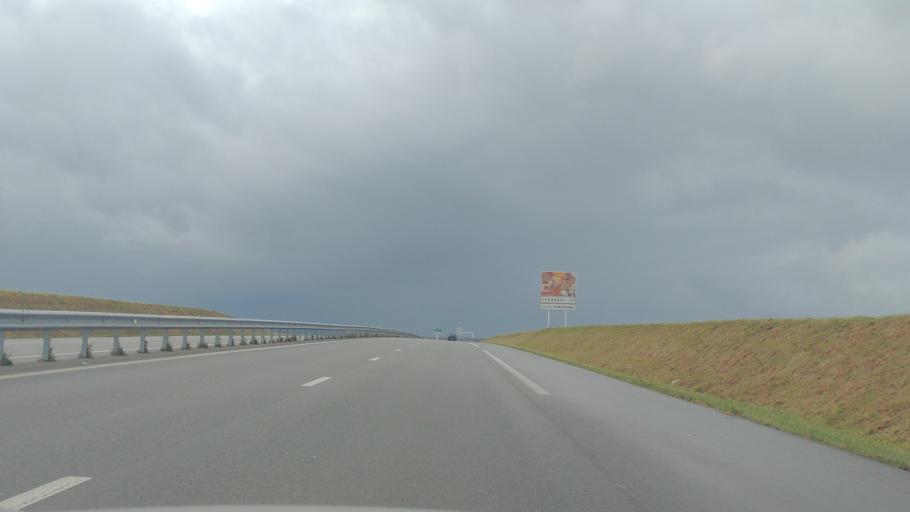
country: FR
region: Picardie
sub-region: Departement de l'Oise
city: Troissereux
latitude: 49.4895
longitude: 2.0468
